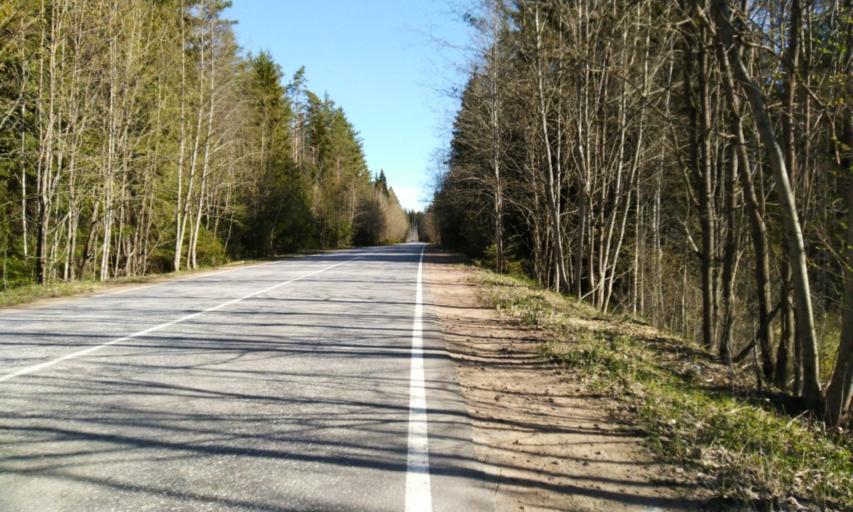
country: RU
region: Leningrad
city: Garbolovo
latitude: 60.3556
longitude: 30.4443
